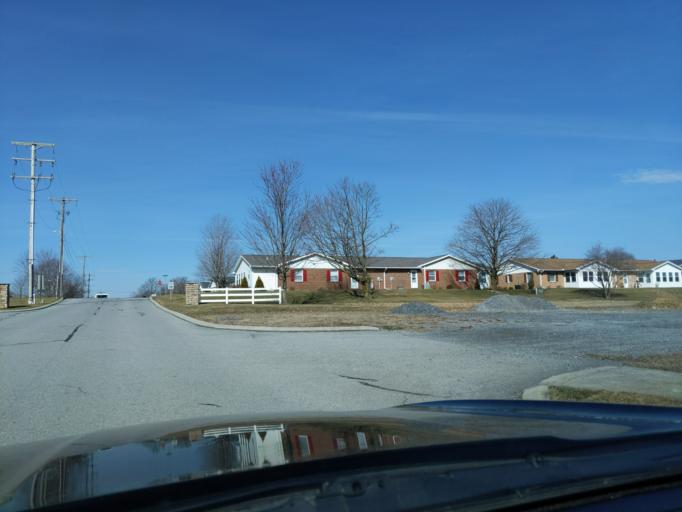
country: US
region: Pennsylvania
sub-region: Blair County
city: Martinsburg
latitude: 40.3028
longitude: -78.3262
